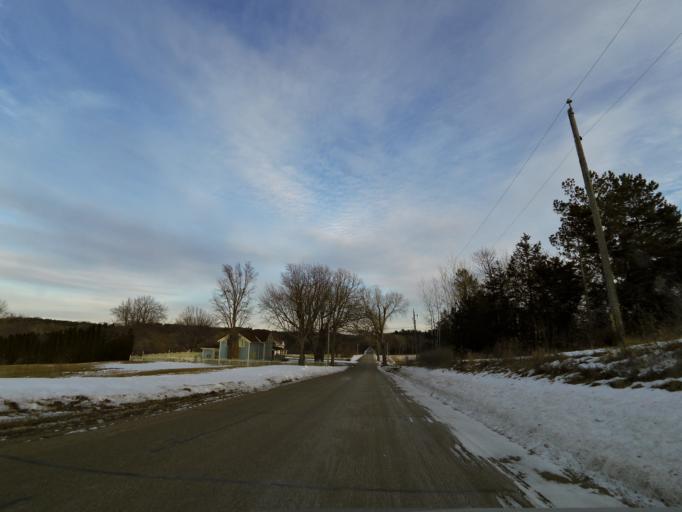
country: US
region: Minnesota
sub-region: Washington County
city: Afton
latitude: 44.9125
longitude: -92.8412
